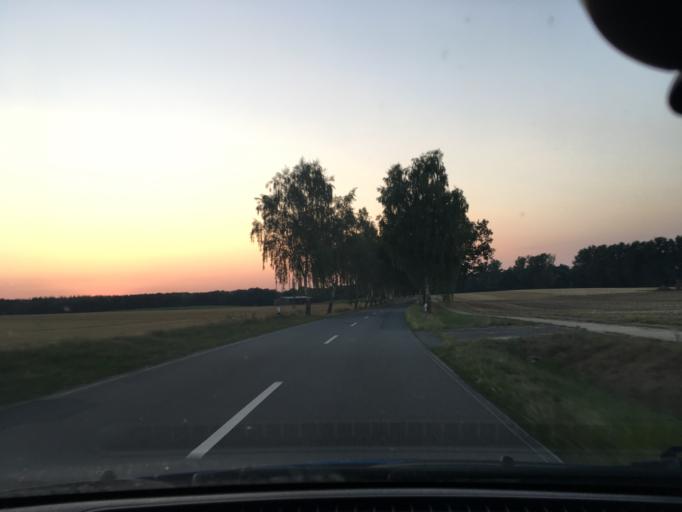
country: DE
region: Lower Saxony
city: Barnstedt
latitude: 53.1521
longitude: 10.3524
